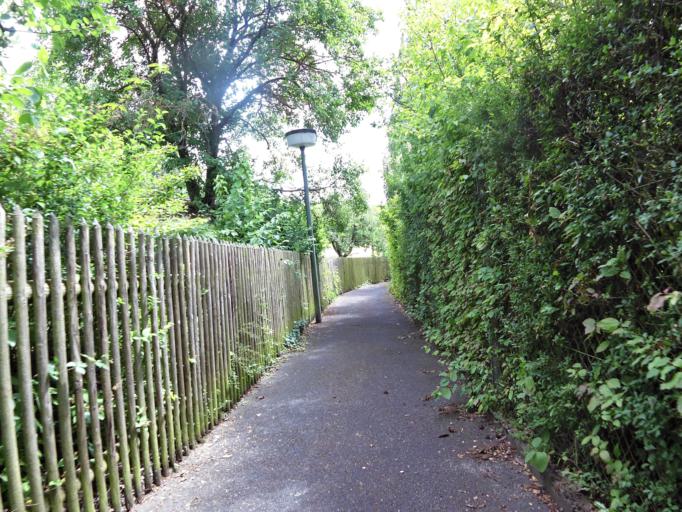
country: DE
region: Bavaria
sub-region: Regierungsbezirk Unterfranken
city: Zell am Main
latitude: 49.8113
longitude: 9.8926
